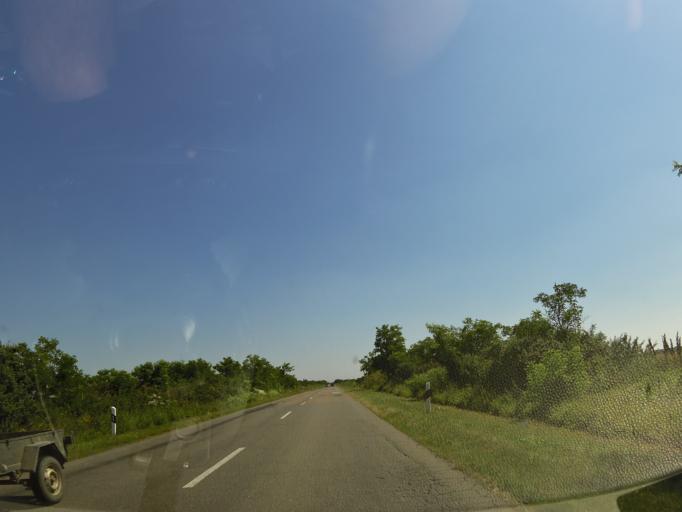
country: HU
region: Jasz-Nagykun-Szolnok
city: Fegyvernek
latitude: 47.2481
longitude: 20.5505
